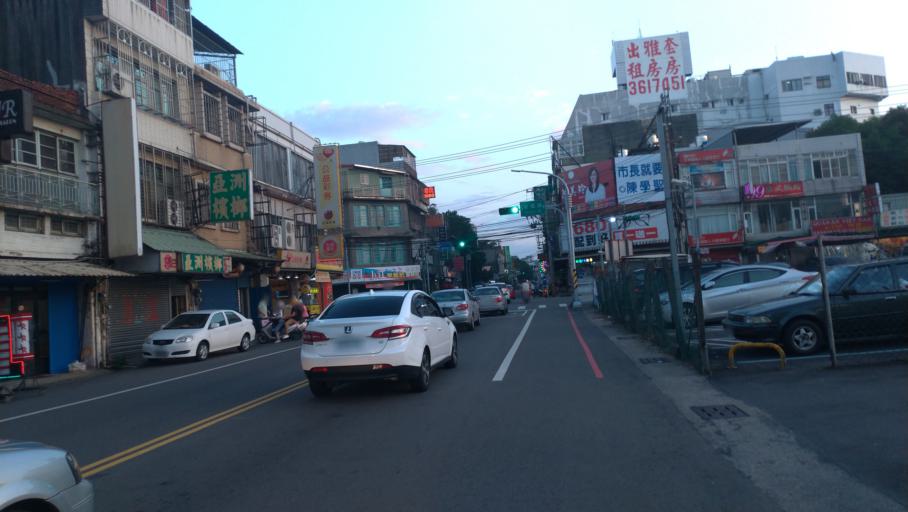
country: TW
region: Taiwan
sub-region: Taoyuan
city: Taoyuan
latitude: 24.9861
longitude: 121.3142
